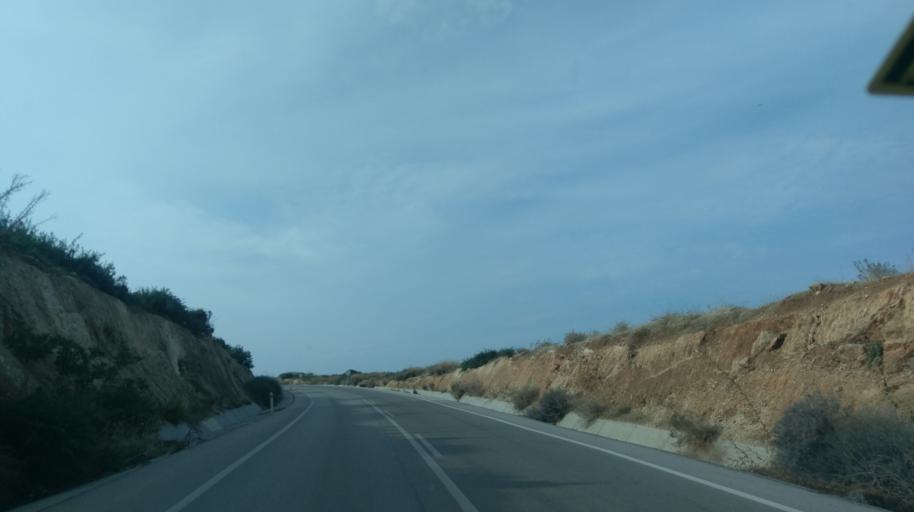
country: CY
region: Ammochostos
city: Trikomo
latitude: 35.4245
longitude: 33.8958
